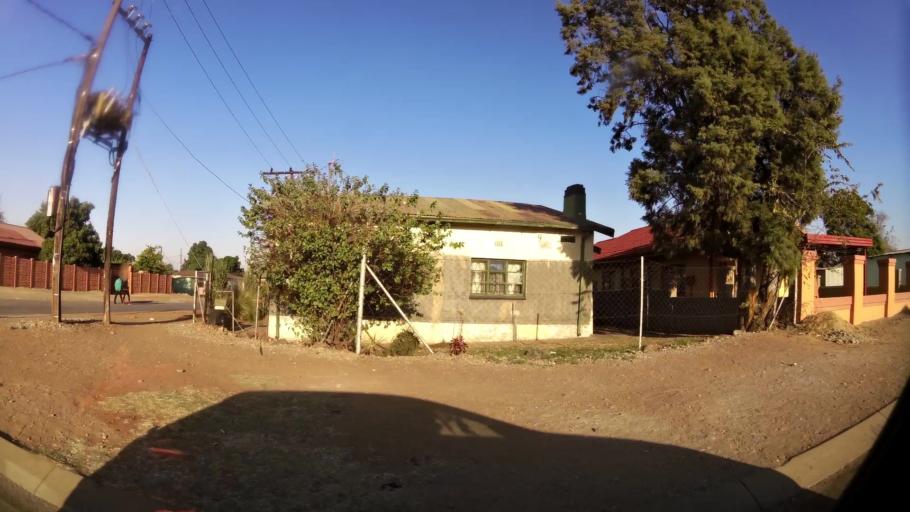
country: ZA
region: North-West
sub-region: Bojanala Platinum District Municipality
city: Rustenburg
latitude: -25.6424
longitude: 27.2149
